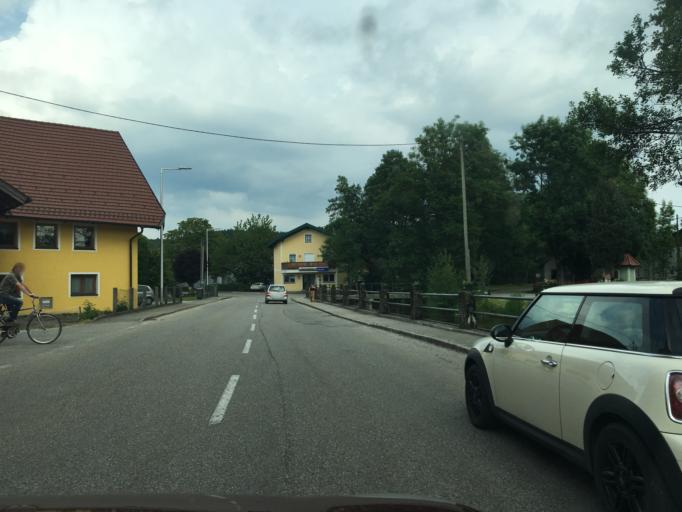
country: AT
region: Upper Austria
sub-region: Politischer Bezirk Braunau am Inn
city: Altheim
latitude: 48.1194
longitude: 13.1581
